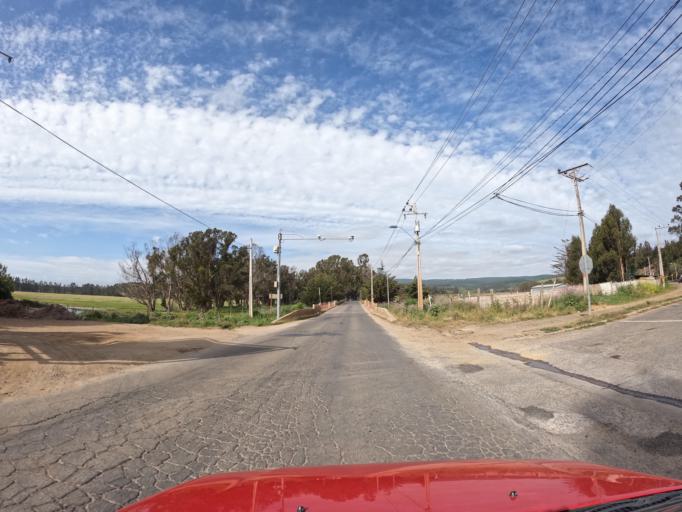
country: CL
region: O'Higgins
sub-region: Provincia de Colchagua
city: Santa Cruz
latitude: -34.3859
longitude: -71.9881
